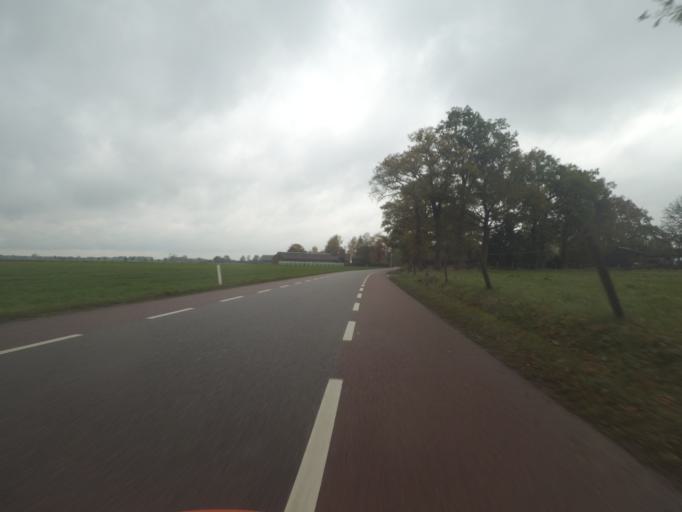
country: NL
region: Gelderland
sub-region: Gemeente Ede
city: Ederveen
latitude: 52.1000
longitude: 5.5677
